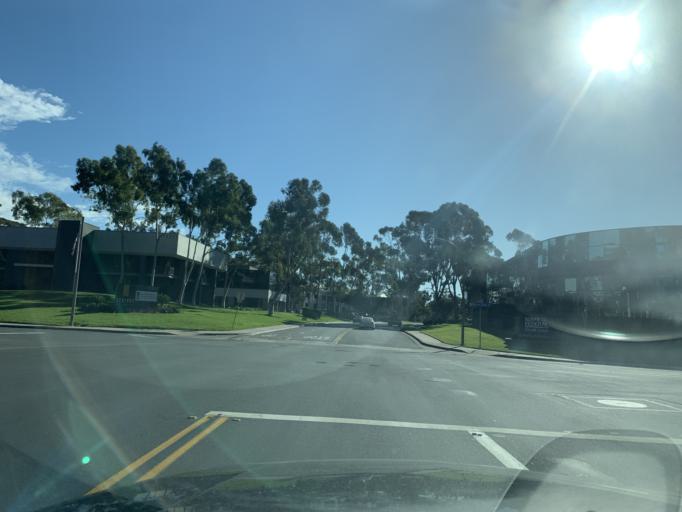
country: US
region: California
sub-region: San Diego County
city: Poway
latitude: 32.9020
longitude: -117.1117
